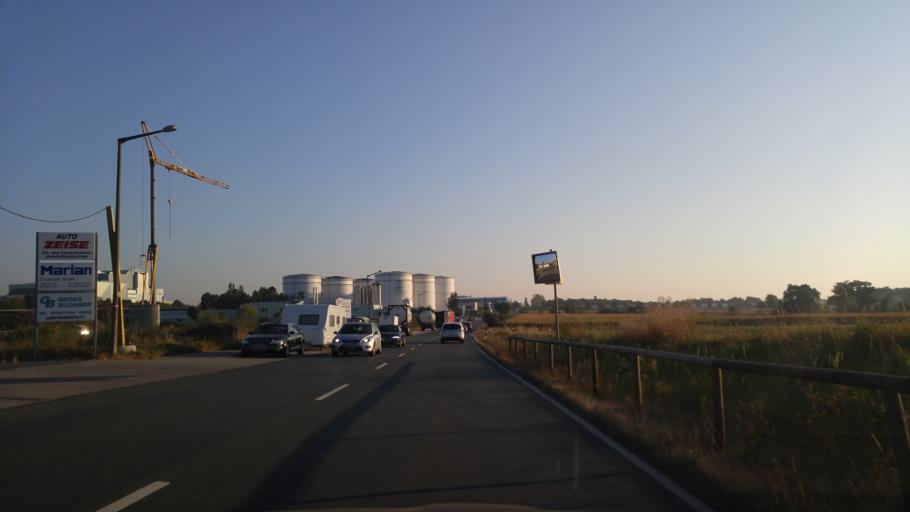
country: DE
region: Bavaria
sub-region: Regierungsbezirk Mittelfranken
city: Furth
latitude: 49.4933
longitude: 10.9468
